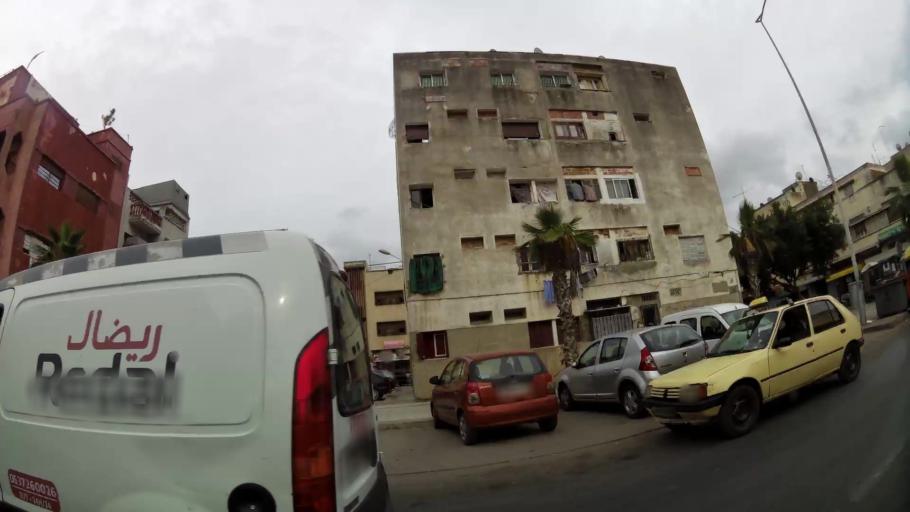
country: MA
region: Rabat-Sale-Zemmour-Zaer
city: Sale
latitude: 34.0483
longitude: -6.7973
